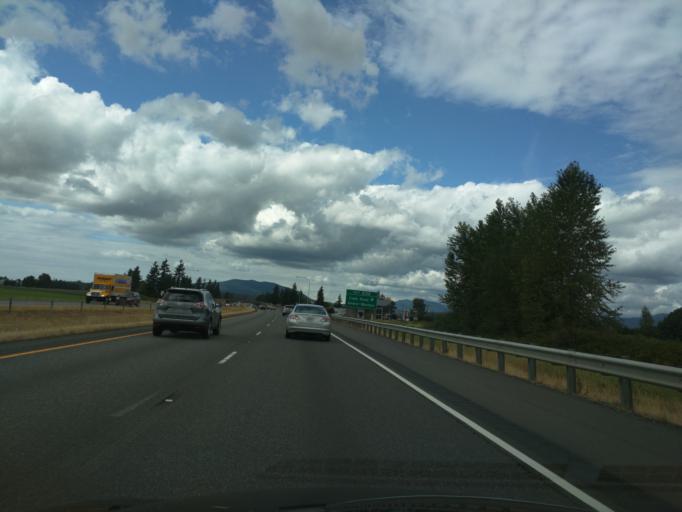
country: US
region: Washington
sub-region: Skagit County
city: Burlington
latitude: 48.5028
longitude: -122.3365
